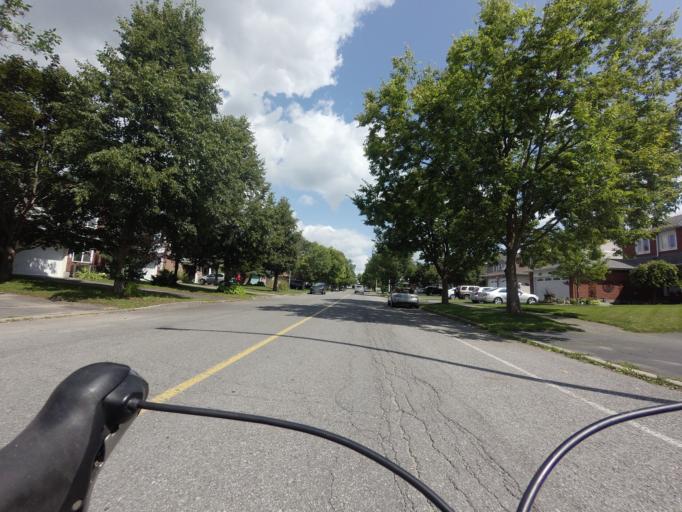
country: CA
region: Ontario
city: Bells Corners
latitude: 45.2766
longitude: -75.8575
